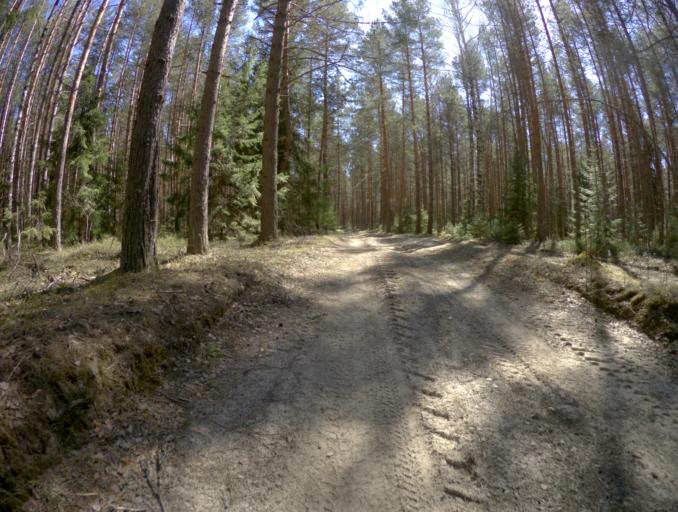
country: RU
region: Vladimir
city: Golovino
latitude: 55.9118
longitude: 40.4354
